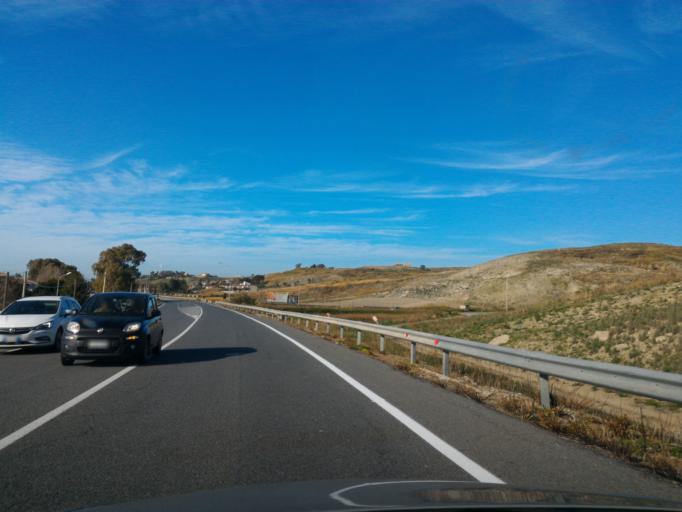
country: IT
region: Calabria
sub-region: Provincia di Crotone
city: Le Castella
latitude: 38.9411
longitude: 16.9810
